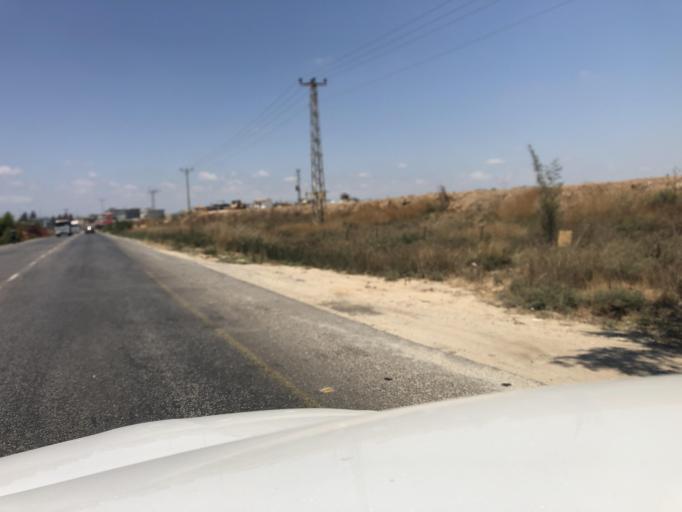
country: IL
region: Central District
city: Jaljulya
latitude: 32.1430
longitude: 34.9575
